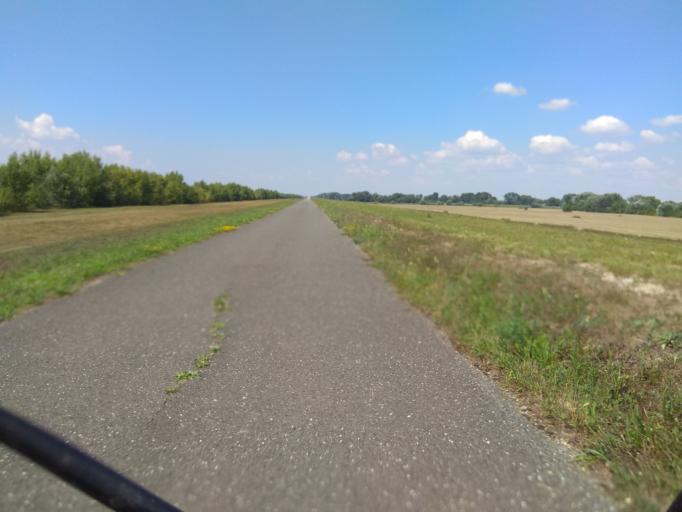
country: SK
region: Trnavsky
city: Gabcikovo
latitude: 47.8270
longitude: 17.6054
